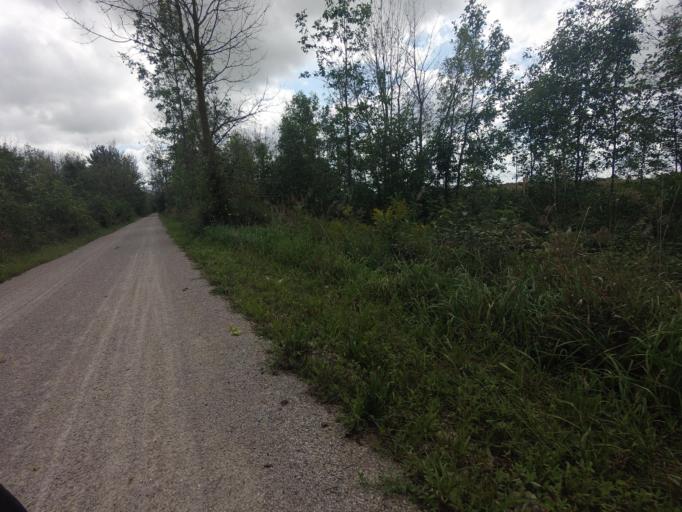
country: CA
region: Ontario
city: North Perth
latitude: 43.5954
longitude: -81.0944
